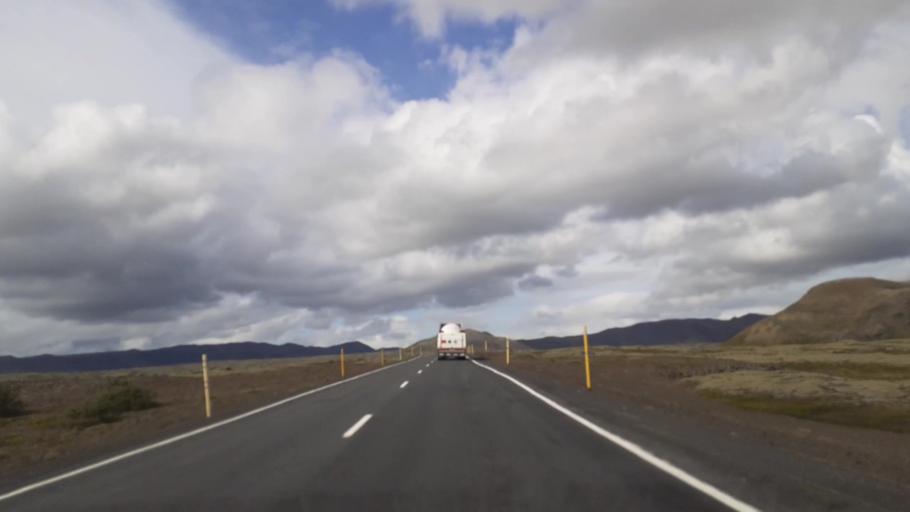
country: IS
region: South
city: THorlakshoefn
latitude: 63.9637
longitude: -21.4532
